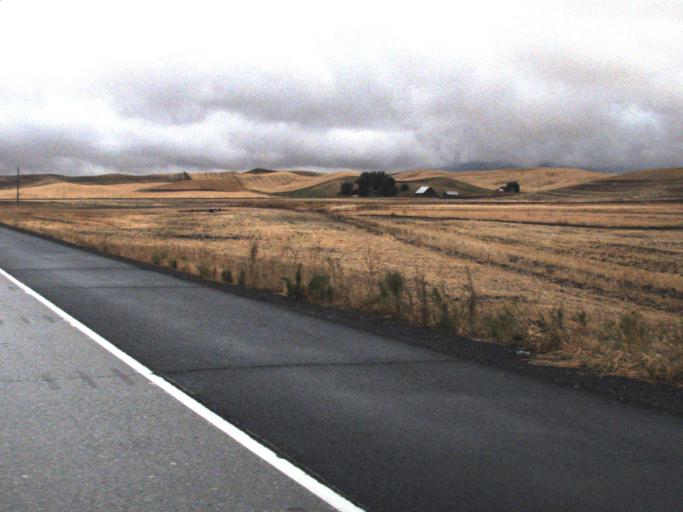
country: US
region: Washington
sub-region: Whitman County
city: Colfax
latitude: 47.0667
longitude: -117.3822
